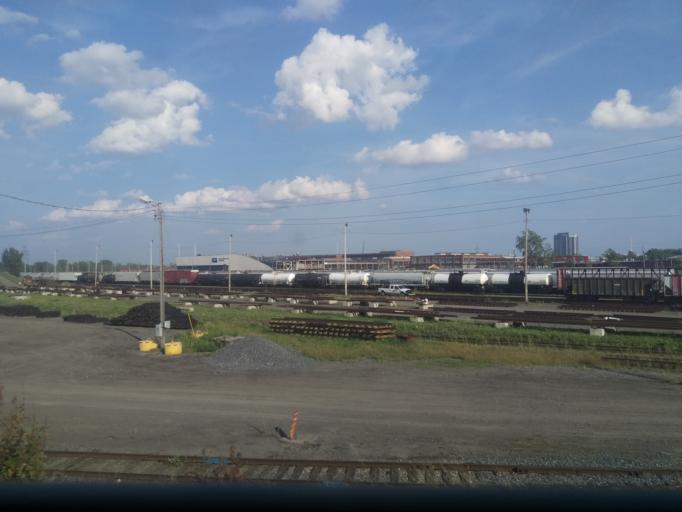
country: CA
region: Quebec
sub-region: Montreal
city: Montreal
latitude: 45.4842
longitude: -73.5562
